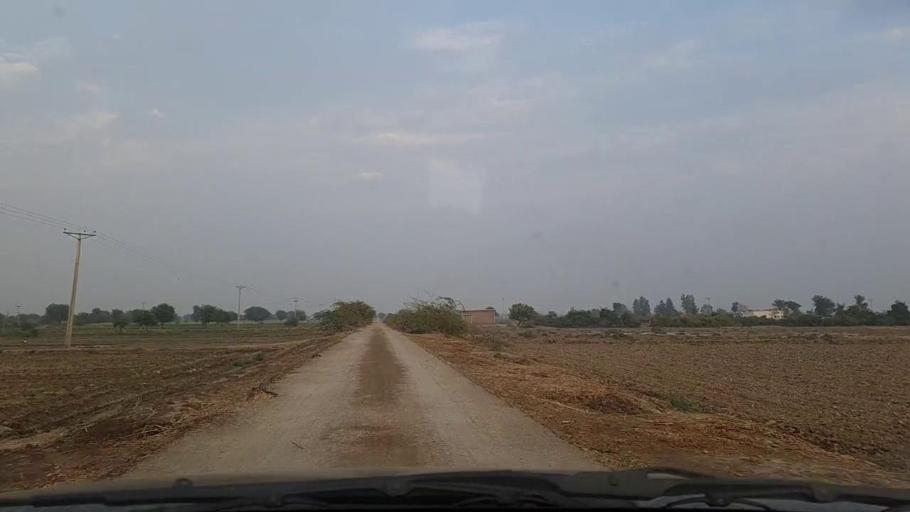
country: PK
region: Sindh
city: Dhoro Naro
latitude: 25.5932
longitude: 69.4927
